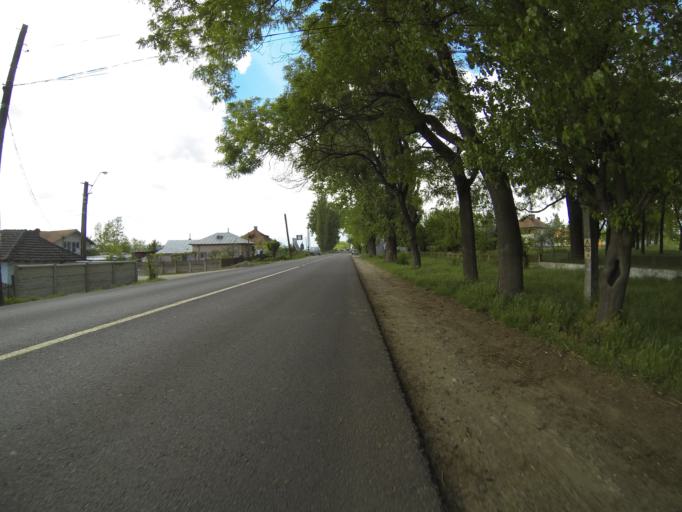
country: RO
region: Dolj
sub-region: Municipiul Craiova
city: Facai
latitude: 44.2749
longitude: 23.8147
